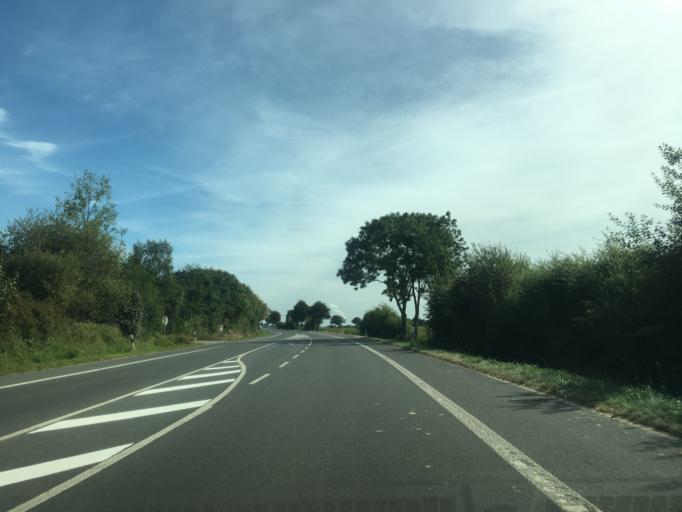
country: DE
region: North Rhine-Westphalia
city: Erkelenz
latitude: 51.0568
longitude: 6.3650
